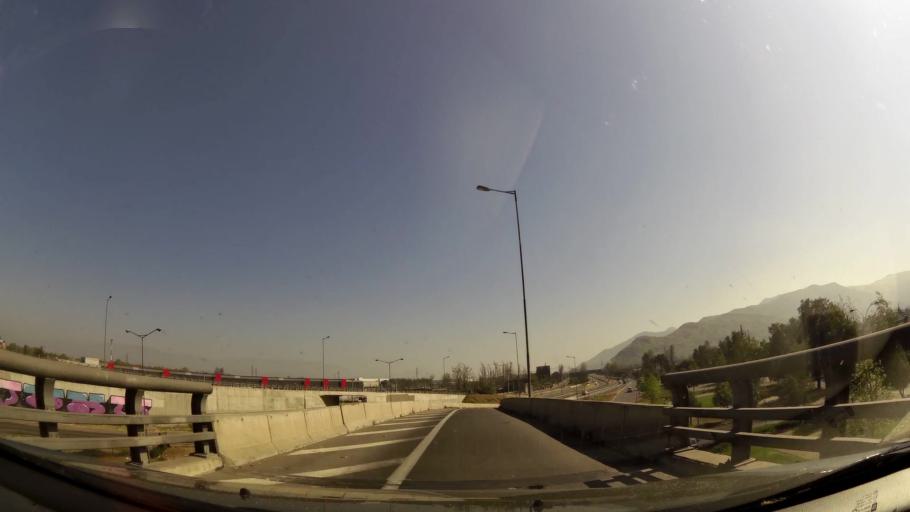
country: CL
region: Santiago Metropolitan
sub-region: Provincia de Santiago
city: Lo Prado
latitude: -33.3653
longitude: -70.6892
